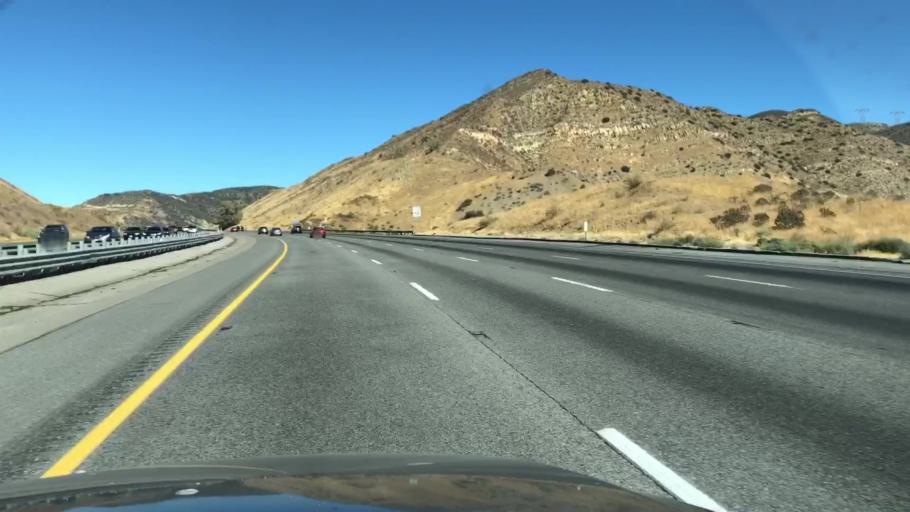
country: US
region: California
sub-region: Los Angeles County
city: Castaic
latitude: 34.6248
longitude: -118.7196
